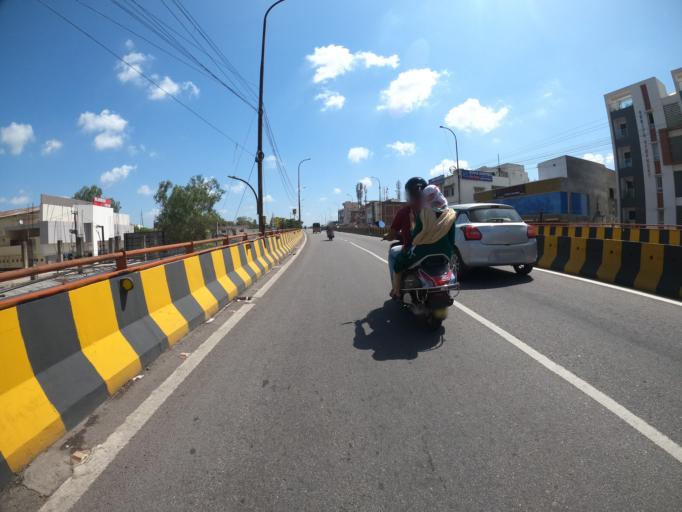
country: IN
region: Telangana
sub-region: Hyderabad
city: Hyderabad
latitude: 17.3760
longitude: 78.4199
